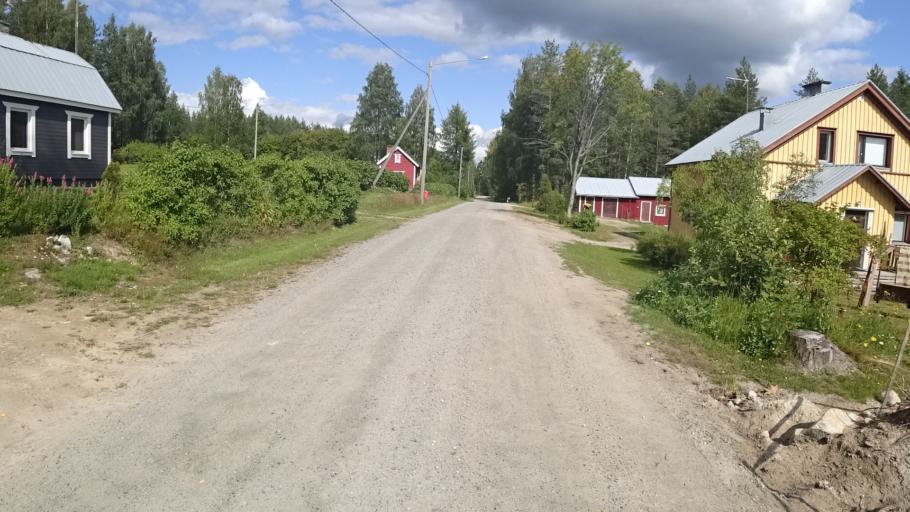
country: FI
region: North Karelia
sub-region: Joensuu
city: Ilomantsi
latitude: 62.6336
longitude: 31.2771
